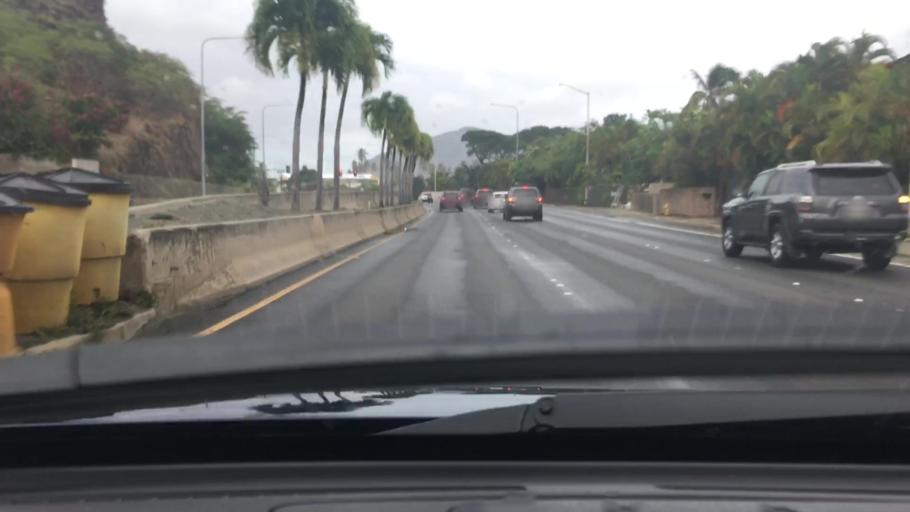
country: US
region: Hawaii
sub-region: Honolulu County
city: Waimanalo Beach
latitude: 21.2825
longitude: -157.7323
